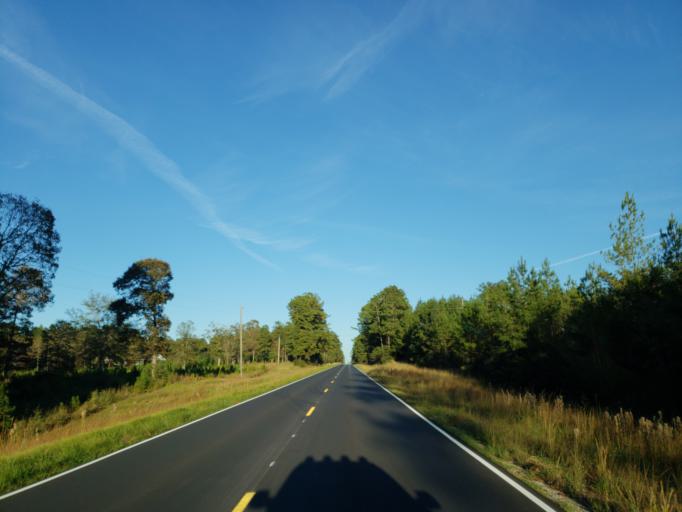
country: US
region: Mississippi
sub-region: Wayne County
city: Belmont
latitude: 31.4124
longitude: -88.6002
